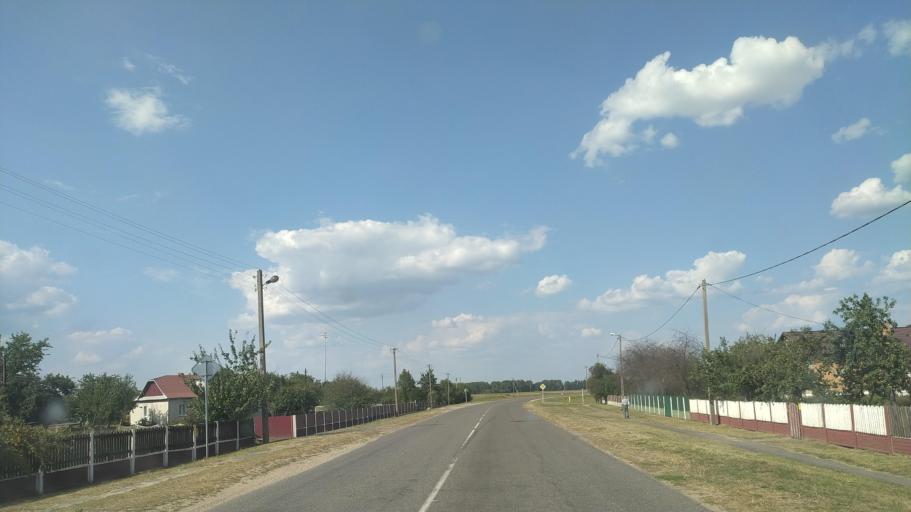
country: BY
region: Brest
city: Drahichyn
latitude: 52.1211
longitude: 25.1167
